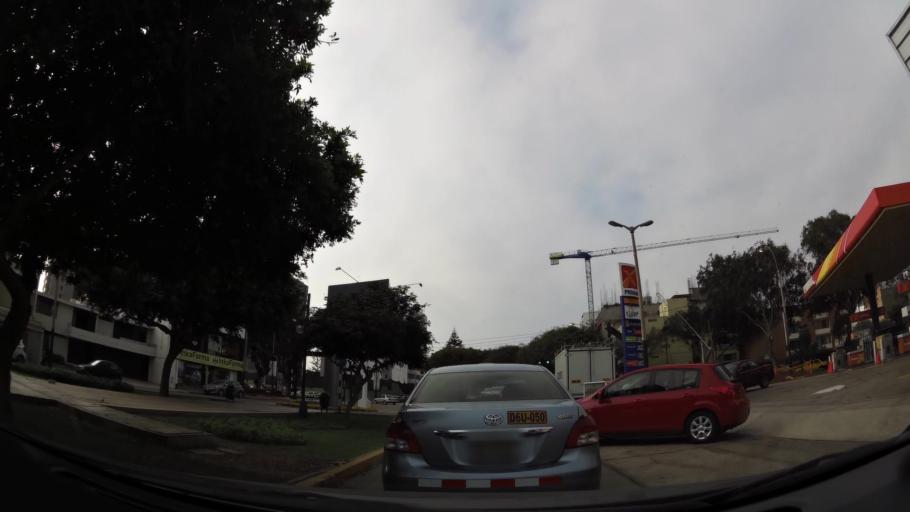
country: PE
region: Lima
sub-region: Lima
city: San Isidro
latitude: -12.1034
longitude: -77.0584
